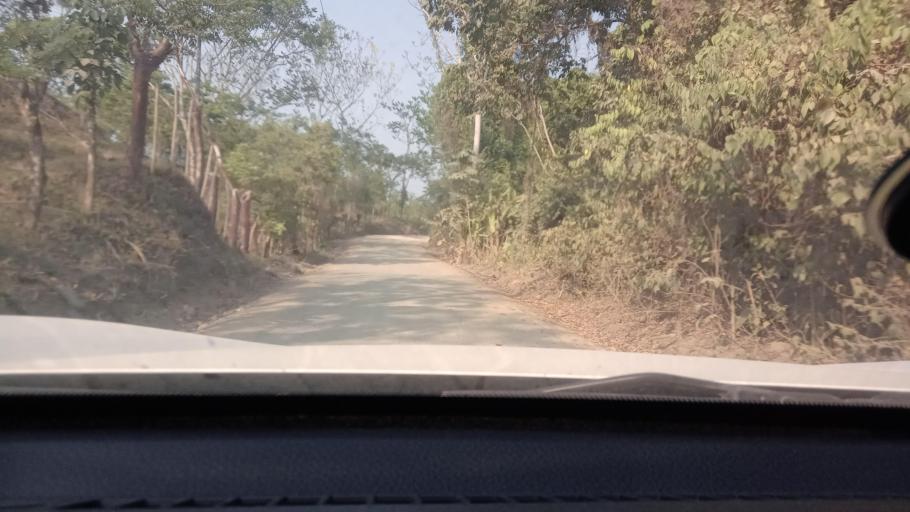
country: MX
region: Tabasco
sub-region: Huimanguillo
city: Francisco Rueda
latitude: 17.6563
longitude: -93.8711
